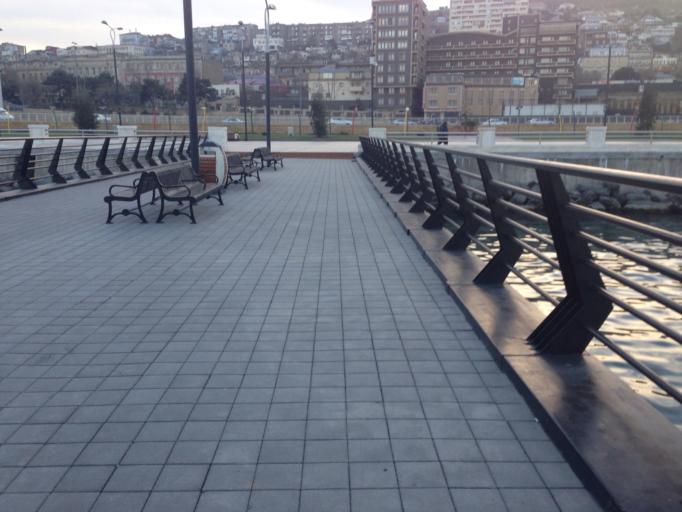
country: AZ
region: Baki
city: Badamdar
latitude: 40.3487
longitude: 49.8391
